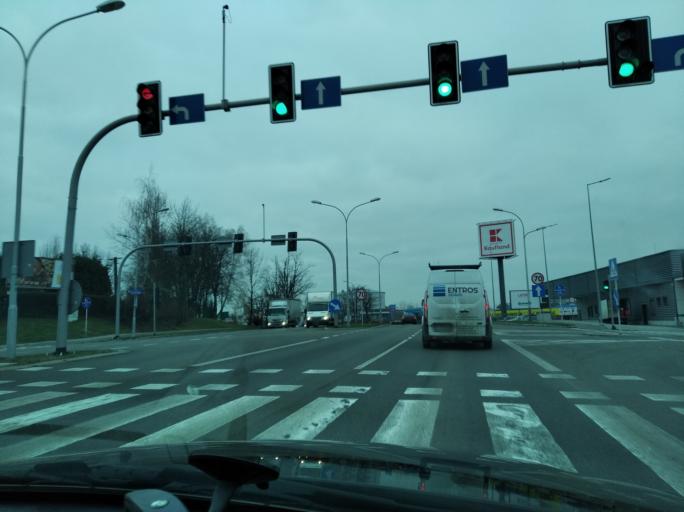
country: PL
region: Subcarpathian Voivodeship
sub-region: Rzeszow
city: Rzeszow
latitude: 50.0499
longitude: 21.9885
